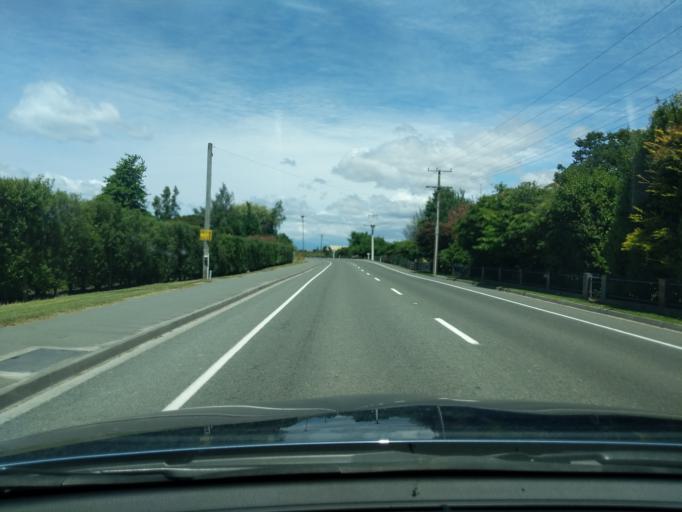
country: NZ
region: Tasman
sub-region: Tasman District
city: Motueka
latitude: -41.0964
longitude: 173.0118
